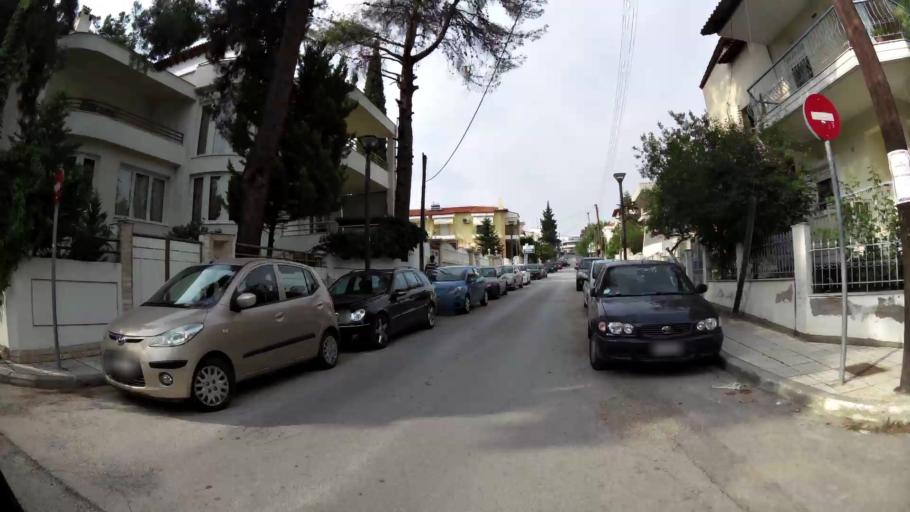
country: GR
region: Central Macedonia
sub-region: Nomos Thessalonikis
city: Oraiokastro
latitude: 40.7291
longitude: 22.9172
